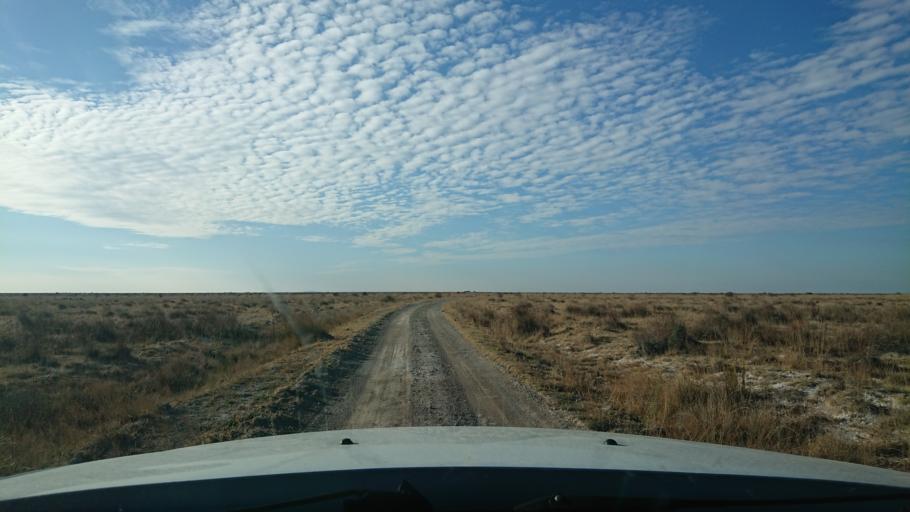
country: TR
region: Aksaray
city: Eskil
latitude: 38.5400
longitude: 33.3391
